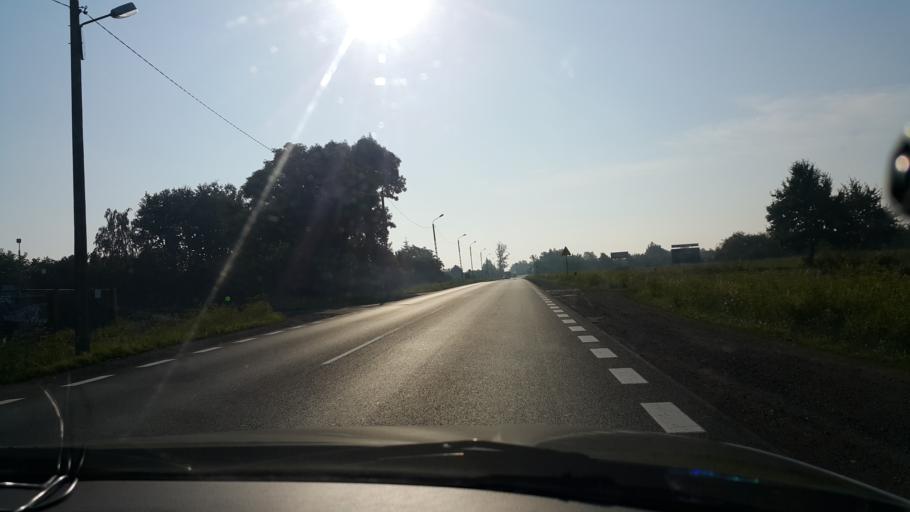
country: PL
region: Masovian Voivodeship
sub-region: Radom
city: Radom
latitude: 51.4135
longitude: 21.2278
